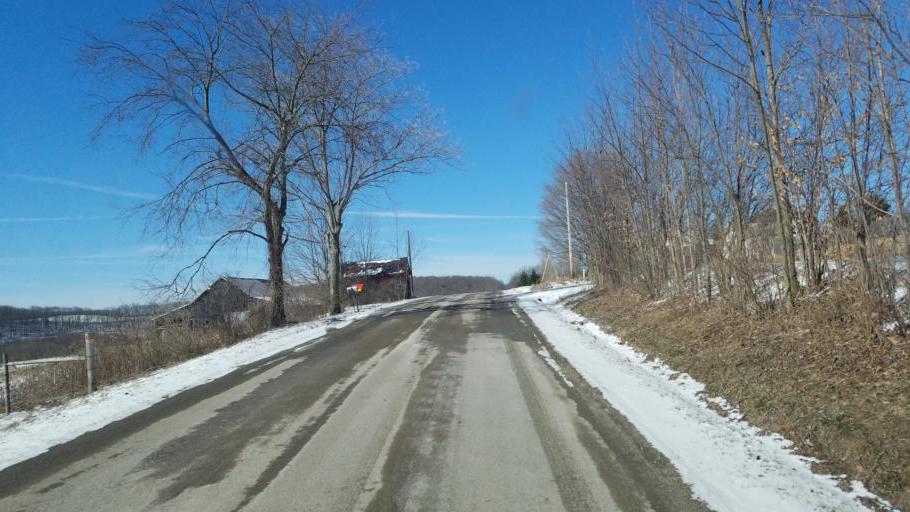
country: US
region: New York
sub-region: Allegany County
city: Wellsville
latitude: 42.0842
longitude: -77.9900
